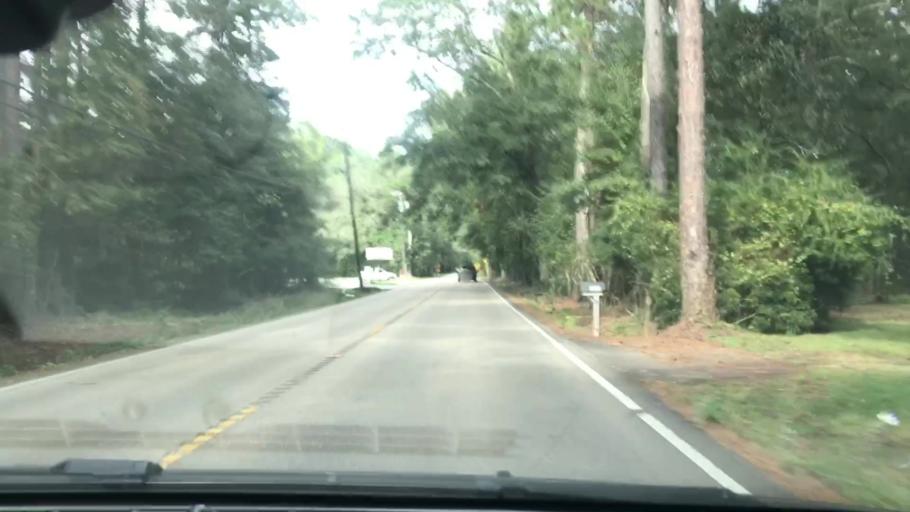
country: US
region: Louisiana
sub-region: Saint Tammany Parish
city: Abita Springs
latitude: 30.4857
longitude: -90.0252
